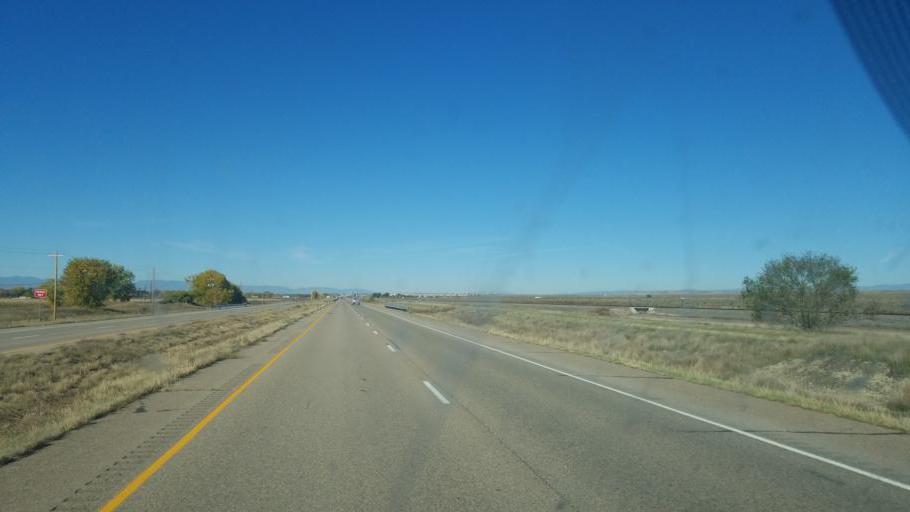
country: US
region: Colorado
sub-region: Pueblo County
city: Pueblo
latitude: 38.2712
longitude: -104.4184
